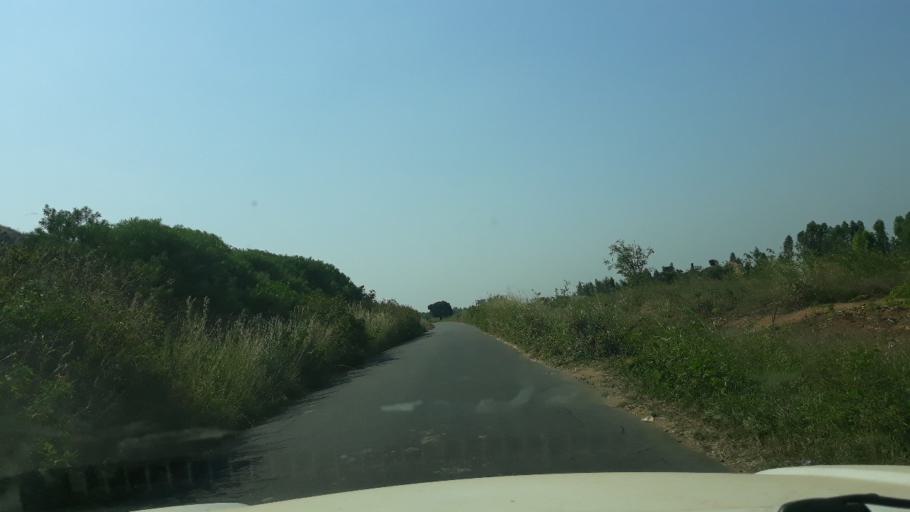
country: CD
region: South Kivu
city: Uvira
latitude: -3.2686
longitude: 29.1614
